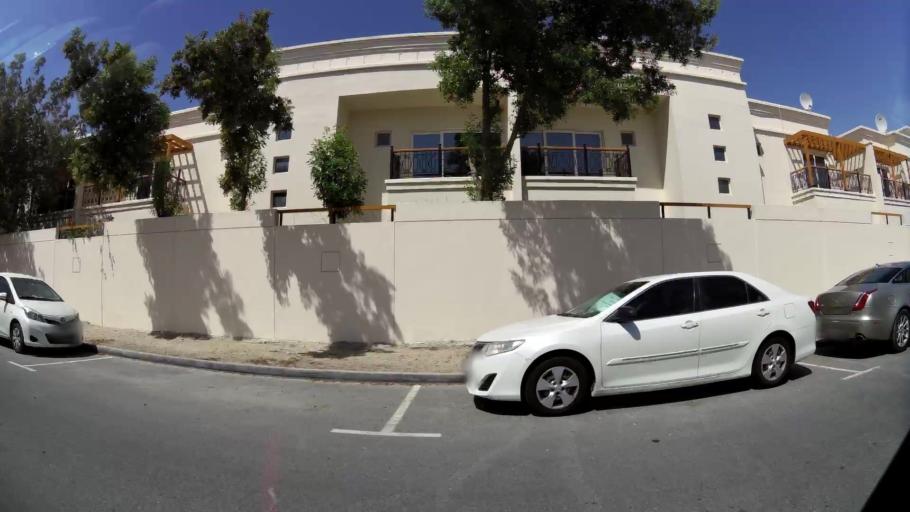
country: AE
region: Dubai
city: Dubai
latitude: 25.1096
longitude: 55.1992
